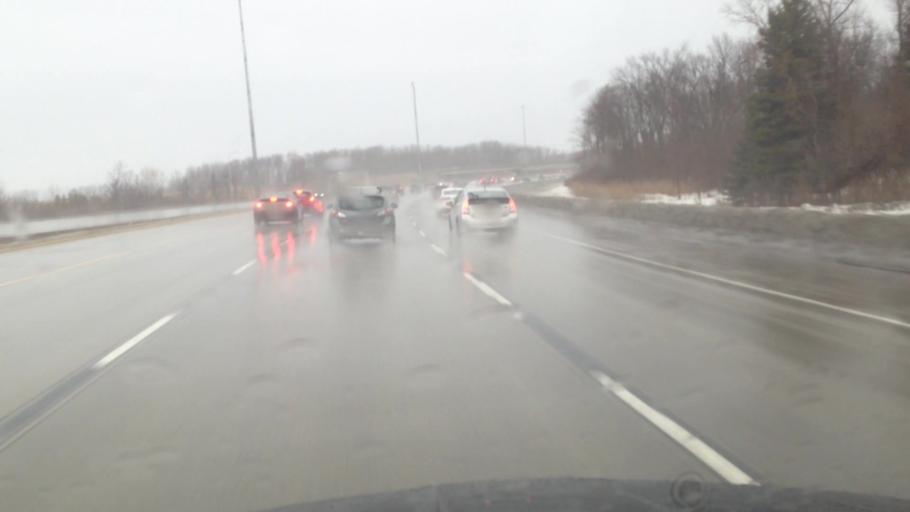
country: CA
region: Quebec
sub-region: Laurentides
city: Saint-Jerome
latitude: 45.7157
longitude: -73.9684
